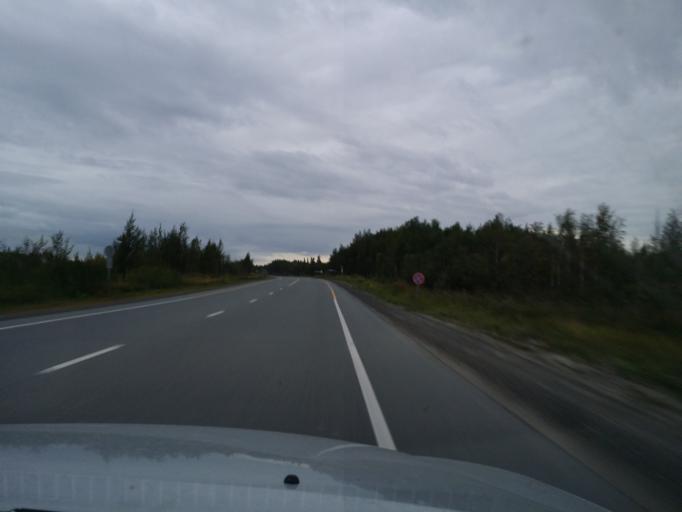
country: RU
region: Khanty-Mansiyskiy Avtonomnyy Okrug
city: Izluchinsk
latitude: 61.0268
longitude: 76.8401
